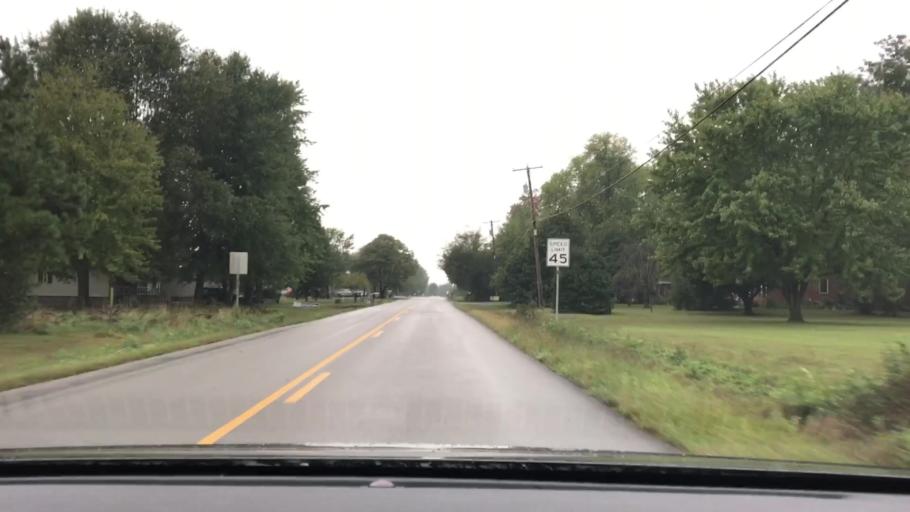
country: US
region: Kentucky
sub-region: Hopkins County
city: Madisonville
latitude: 37.3519
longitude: -87.3961
